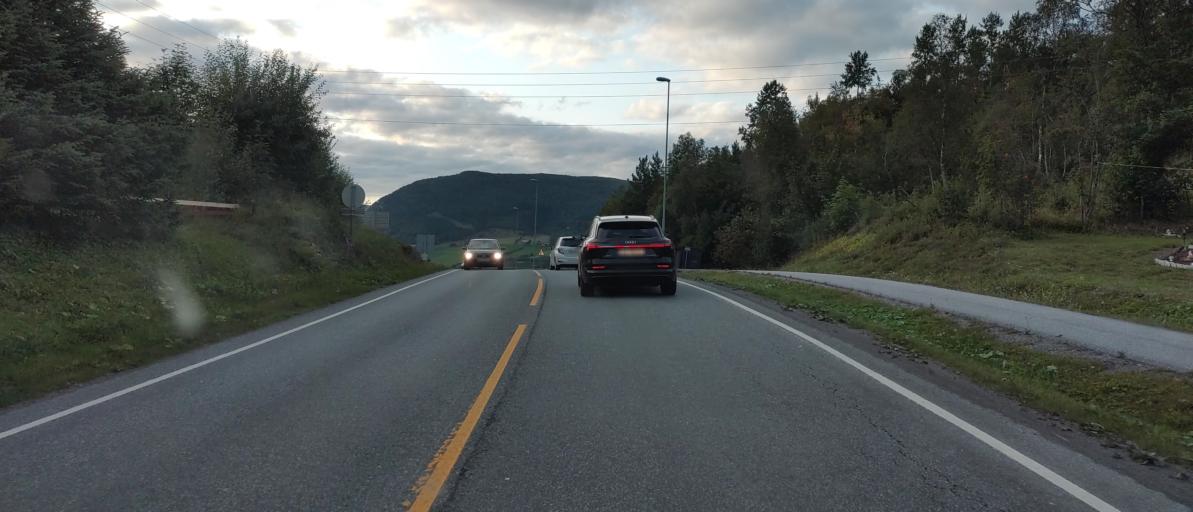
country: NO
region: More og Romsdal
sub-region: Molde
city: Molde
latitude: 62.7935
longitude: 7.2316
